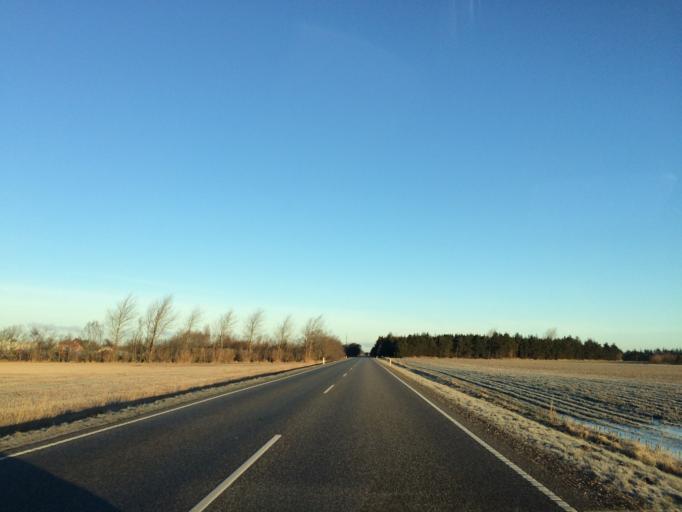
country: DK
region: Central Jutland
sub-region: Holstebro Kommune
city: Ulfborg
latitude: 56.3915
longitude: 8.3218
